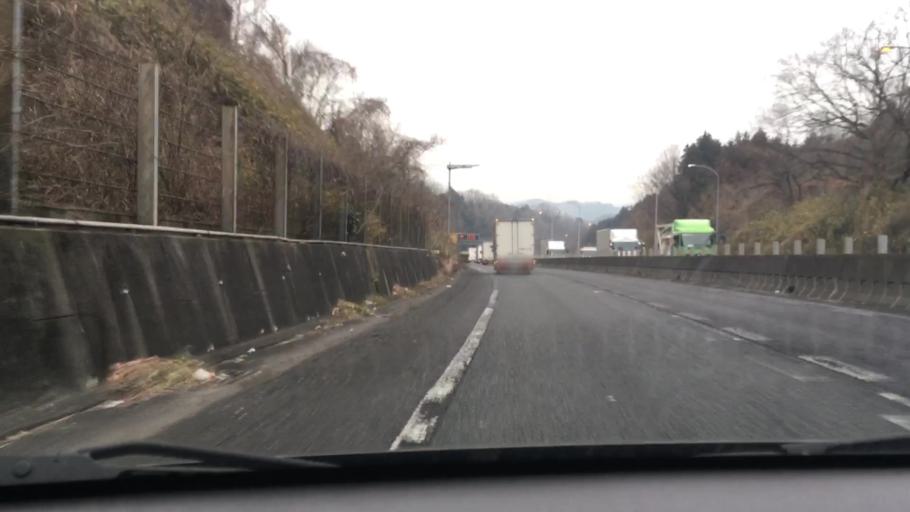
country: JP
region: Mie
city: Nabari
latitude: 34.6862
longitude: 136.0472
